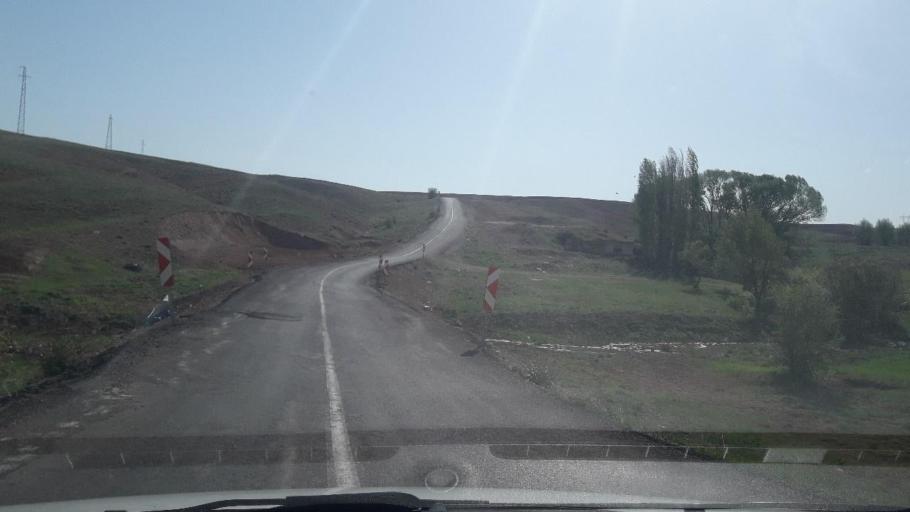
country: TR
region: Sivas
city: Alacahan
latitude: 39.0759
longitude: 37.5476
